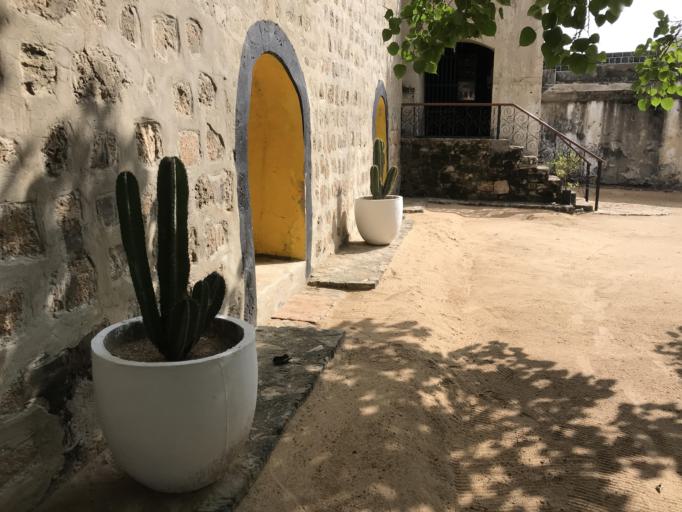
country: LK
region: Northern Province
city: Jaffna
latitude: 9.7116
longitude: 79.8479
